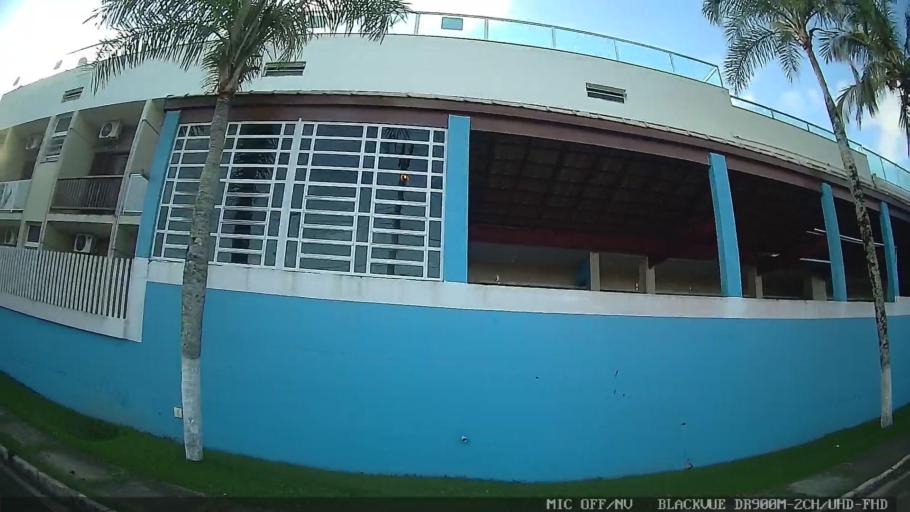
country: BR
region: Sao Paulo
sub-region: Peruibe
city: Peruibe
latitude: -24.2906
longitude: -46.9597
